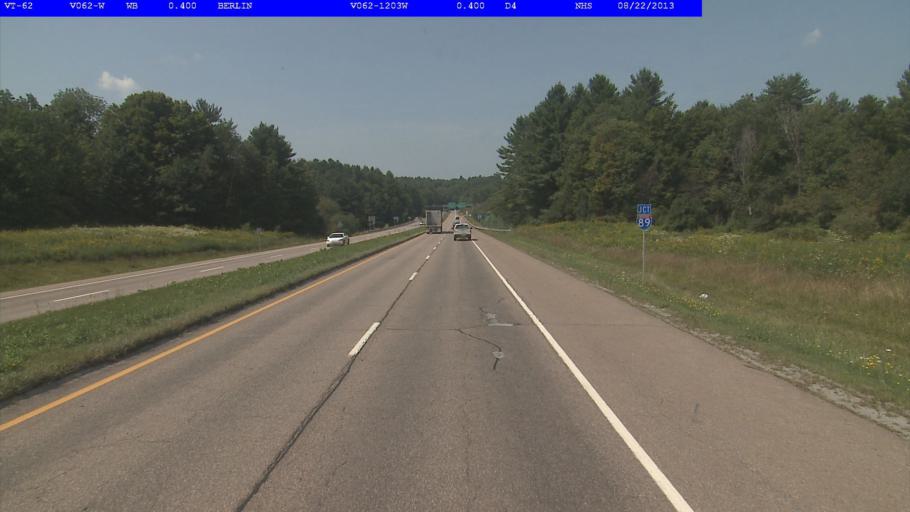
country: US
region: Vermont
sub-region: Washington County
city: Montpelier
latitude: 44.2143
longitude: -72.5766
